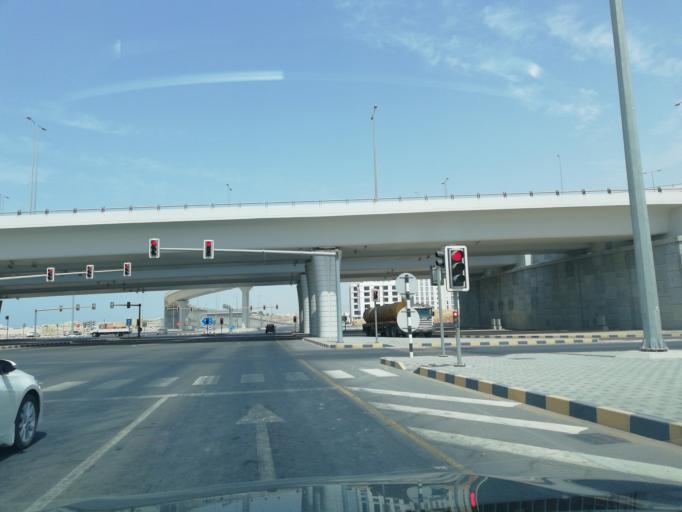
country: OM
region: Muhafazat Masqat
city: Bawshar
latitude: 23.5827
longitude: 58.3318
